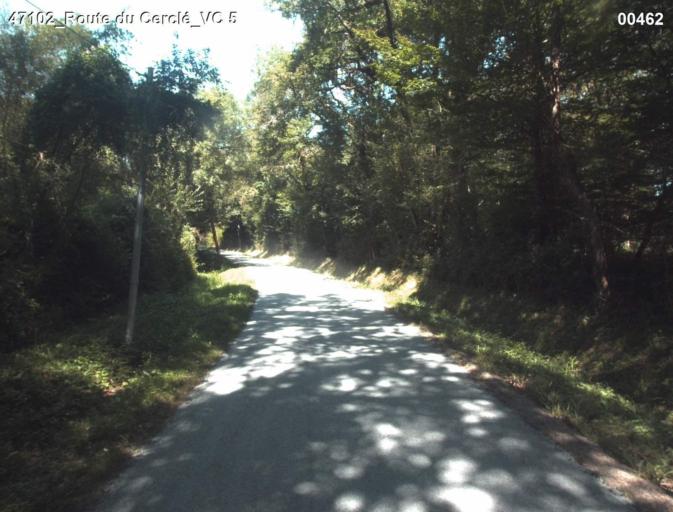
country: FR
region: Aquitaine
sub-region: Departement du Lot-et-Garonne
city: Laplume
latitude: 44.0730
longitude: 0.4566
